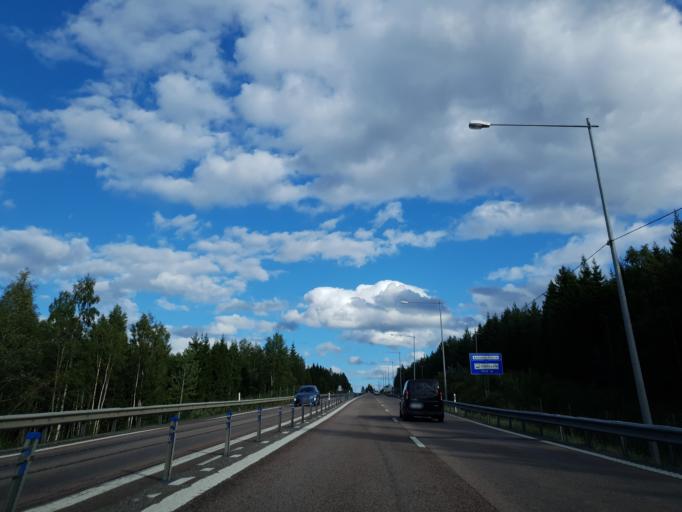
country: SE
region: Vaesternorrland
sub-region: Haernoesands Kommun
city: Haernoesand
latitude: 62.6570
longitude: 17.8705
